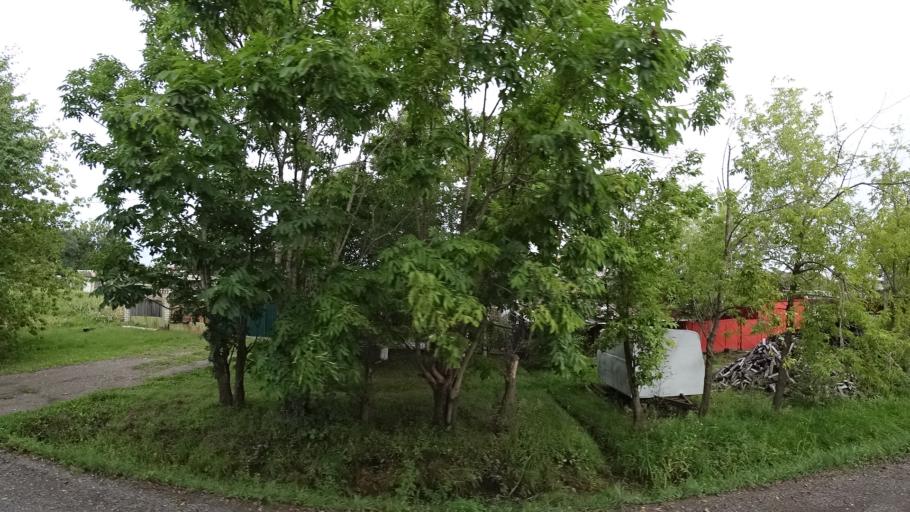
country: RU
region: Primorskiy
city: Chernigovka
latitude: 44.3351
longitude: 132.5775
